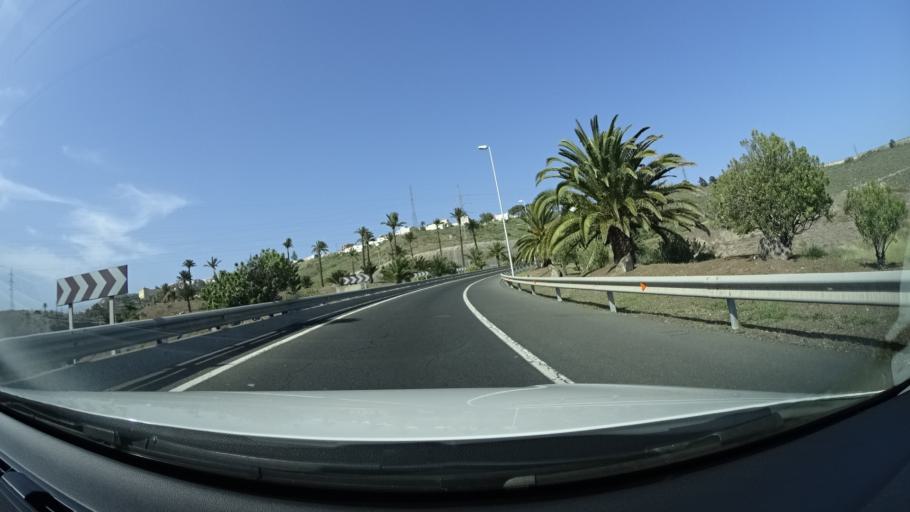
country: ES
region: Canary Islands
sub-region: Provincia de Las Palmas
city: Las Palmas de Gran Canaria
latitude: 28.0760
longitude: -15.4394
